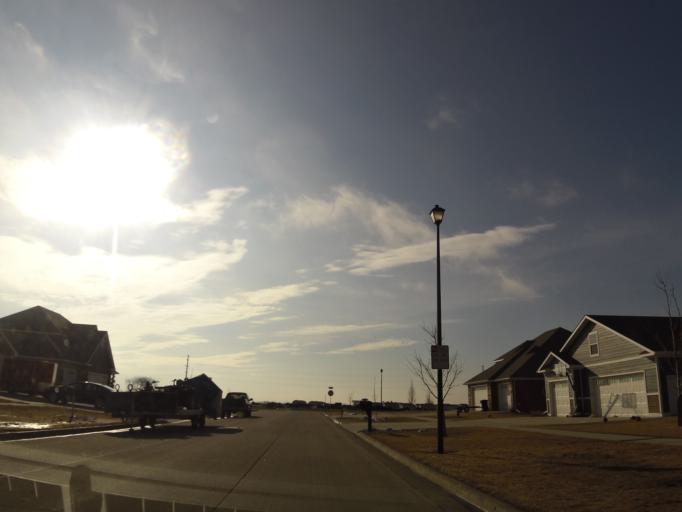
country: US
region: North Dakota
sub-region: Grand Forks County
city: Grand Forks
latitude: 47.8787
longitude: -97.0630
